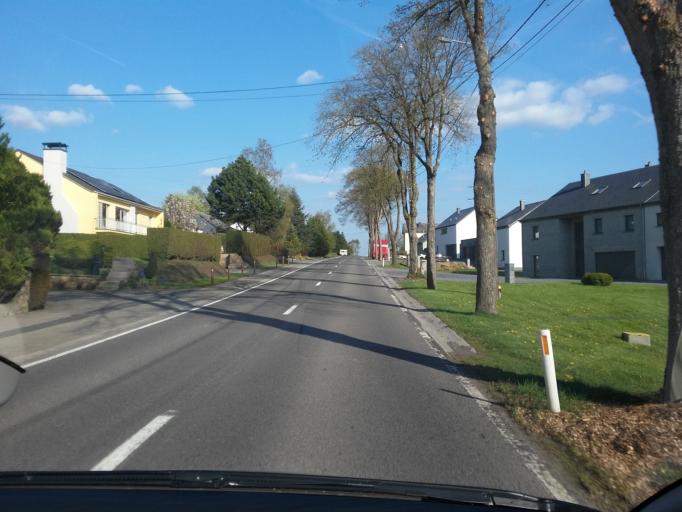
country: BE
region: Wallonia
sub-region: Province du Luxembourg
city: Arlon
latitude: 49.6956
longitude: 5.7597
